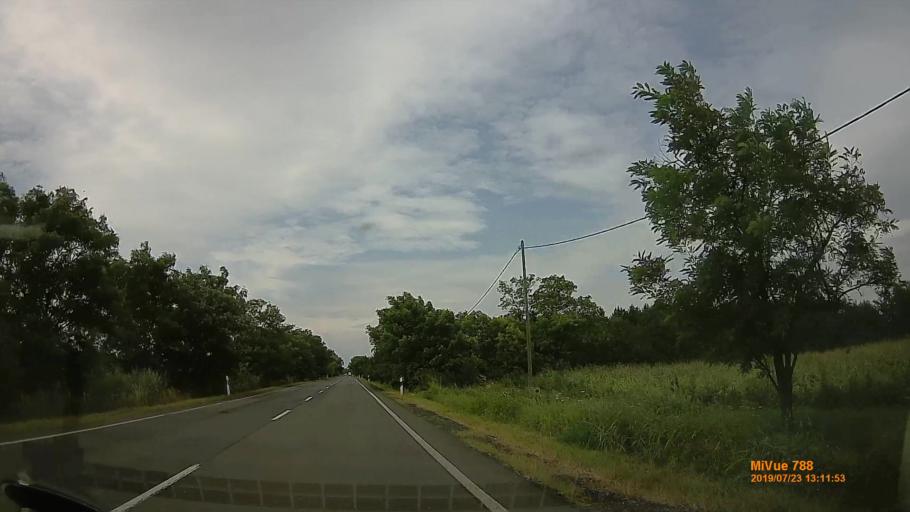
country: HU
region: Szabolcs-Szatmar-Bereg
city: Tiszavasvari
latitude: 47.9293
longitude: 21.2627
